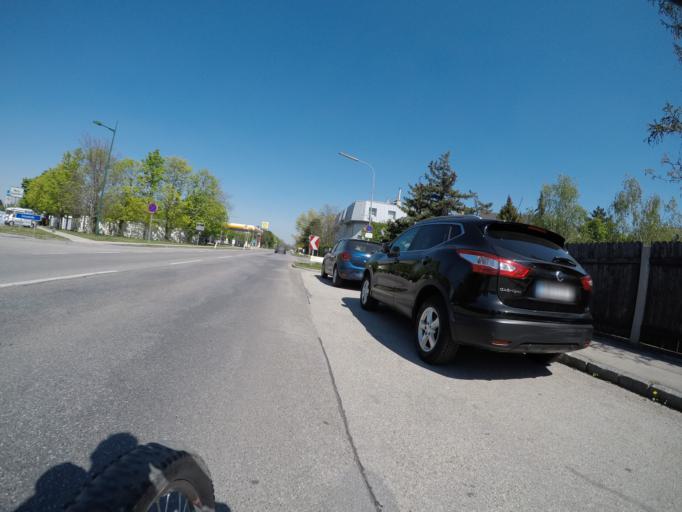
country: AT
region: Lower Austria
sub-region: Politischer Bezirk Modling
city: Wiener Neudorf
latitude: 48.0903
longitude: 16.3083
